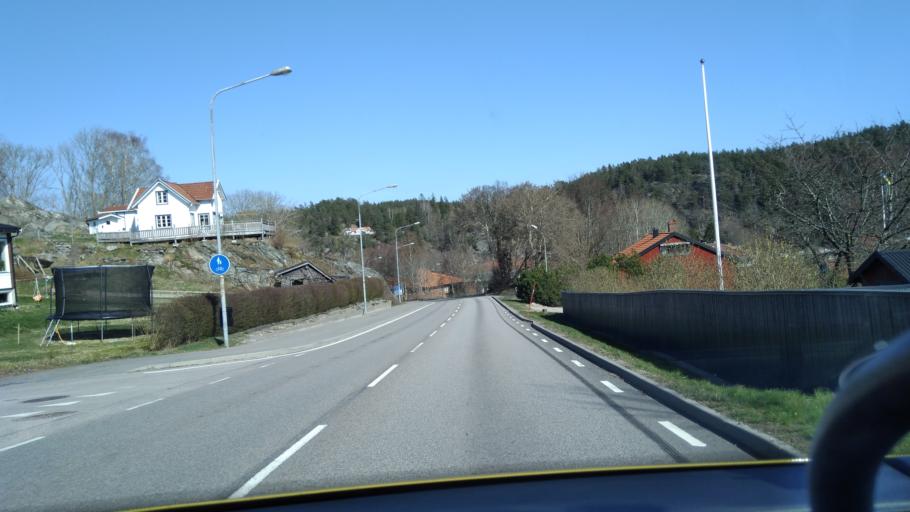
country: SE
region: Vaestra Goetaland
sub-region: Orust
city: Henan
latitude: 58.2345
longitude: 11.6754
